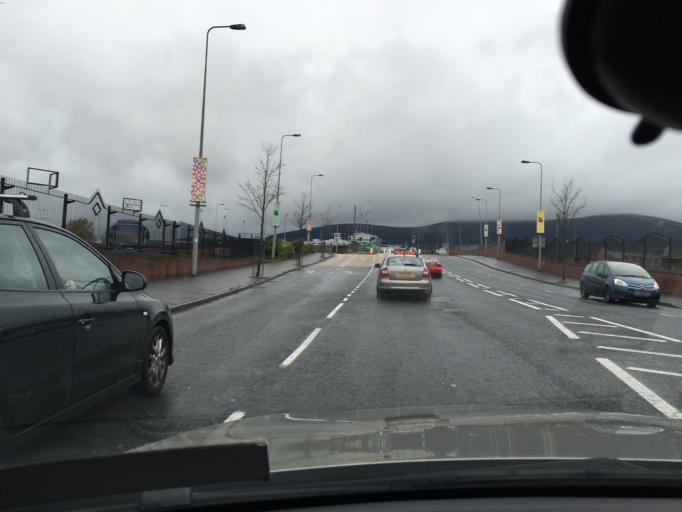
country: GB
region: Northern Ireland
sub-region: City of Belfast
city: Belfast
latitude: 54.5955
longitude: -5.9399
